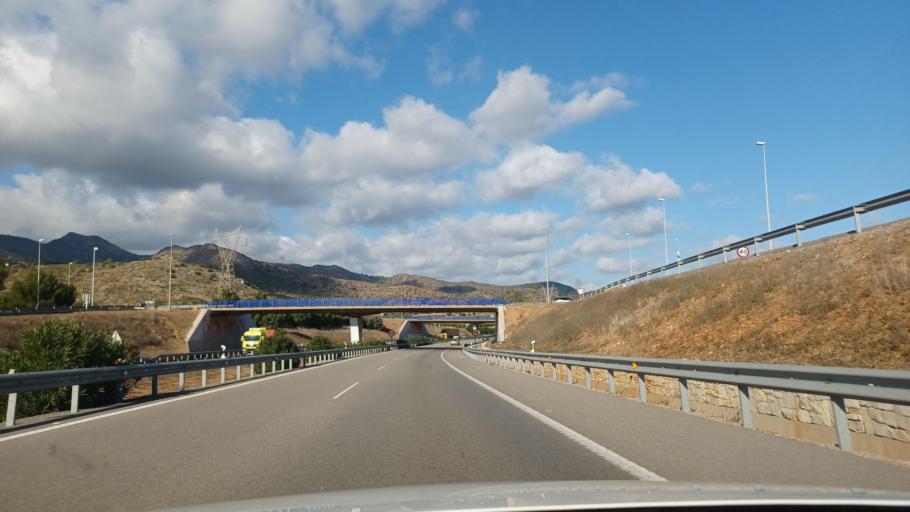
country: ES
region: Valencia
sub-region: Provincia de Castello
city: Villavieja
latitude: 39.8288
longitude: -0.2058
